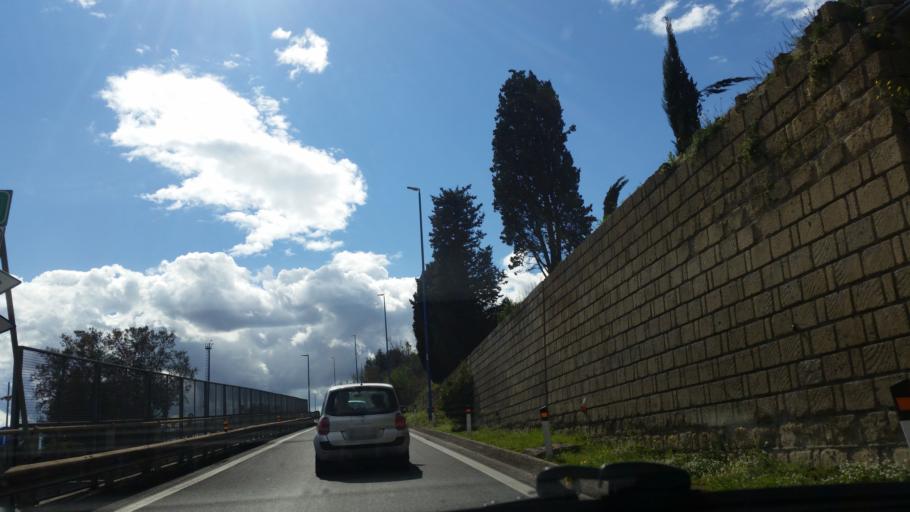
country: IT
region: Campania
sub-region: Provincia di Napoli
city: Napoli
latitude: 40.8660
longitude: 14.2418
